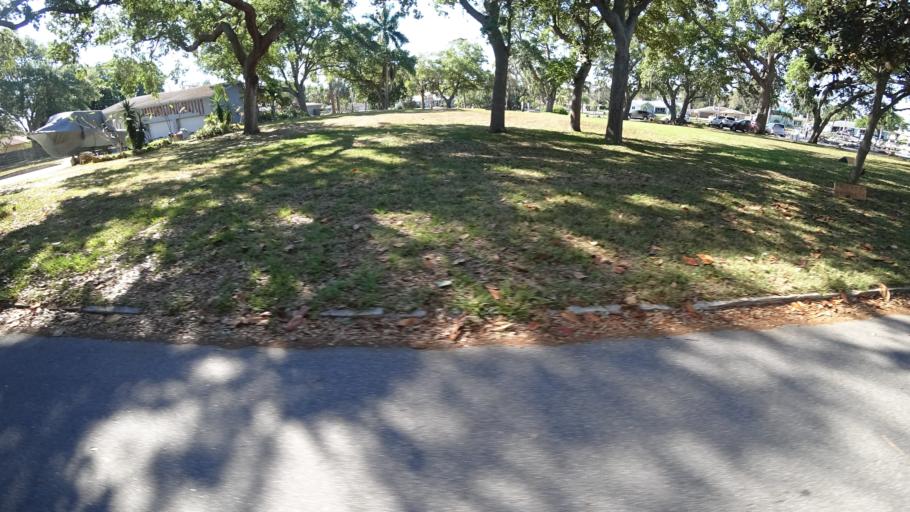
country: US
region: Florida
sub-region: Manatee County
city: West Bradenton
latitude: 27.4873
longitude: -82.6421
